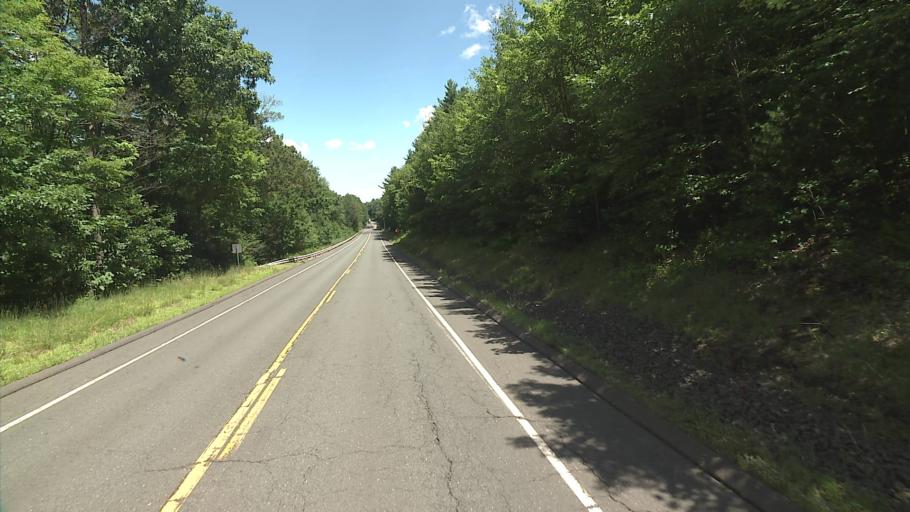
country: US
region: Connecticut
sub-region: Hartford County
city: North Granby
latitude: 41.9517
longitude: -72.8871
